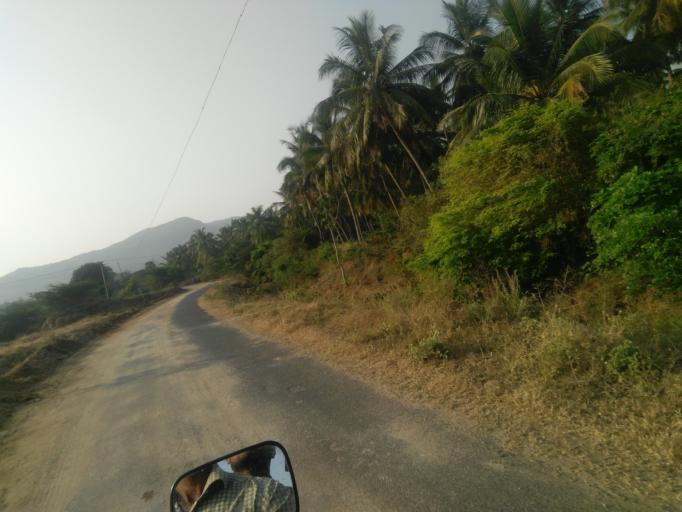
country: IN
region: Tamil Nadu
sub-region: Coimbatore
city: Karamadai
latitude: 11.2136
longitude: 76.8914
